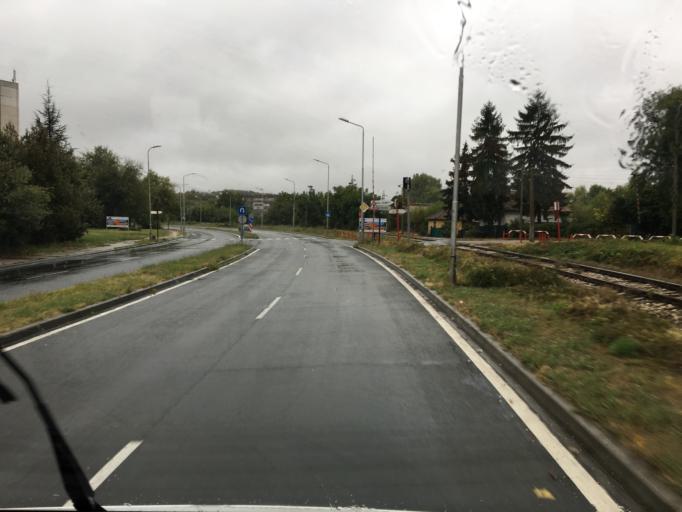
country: BG
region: Lovech
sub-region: Obshtina Lovech
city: Lovech
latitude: 43.1590
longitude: 24.7145
